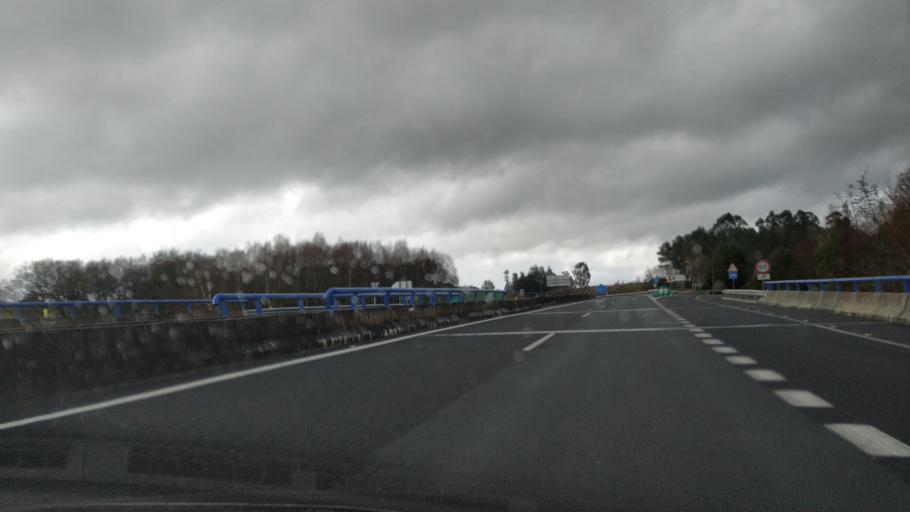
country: ES
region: Galicia
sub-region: Provincia de Pontevedra
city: Silleda
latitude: 42.7131
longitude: -8.2365
